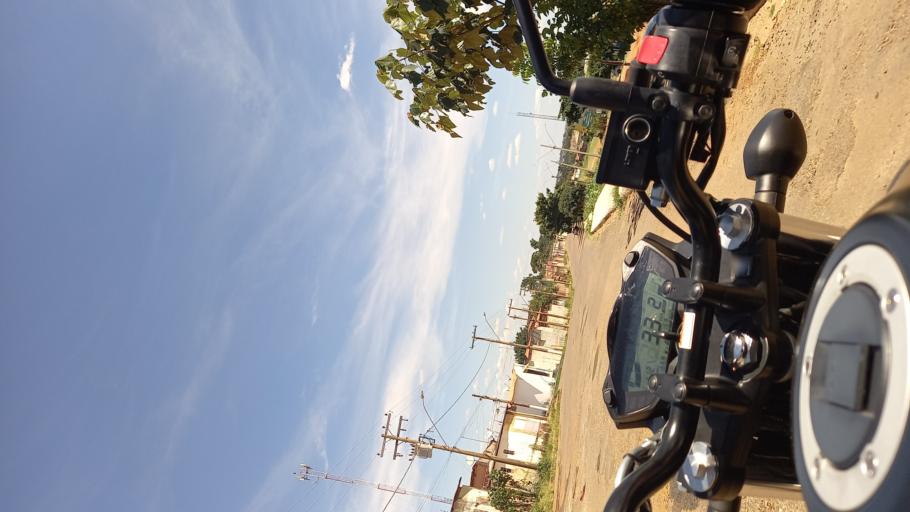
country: BR
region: Goias
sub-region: Luziania
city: Luziania
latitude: -16.1043
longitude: -47.9312
